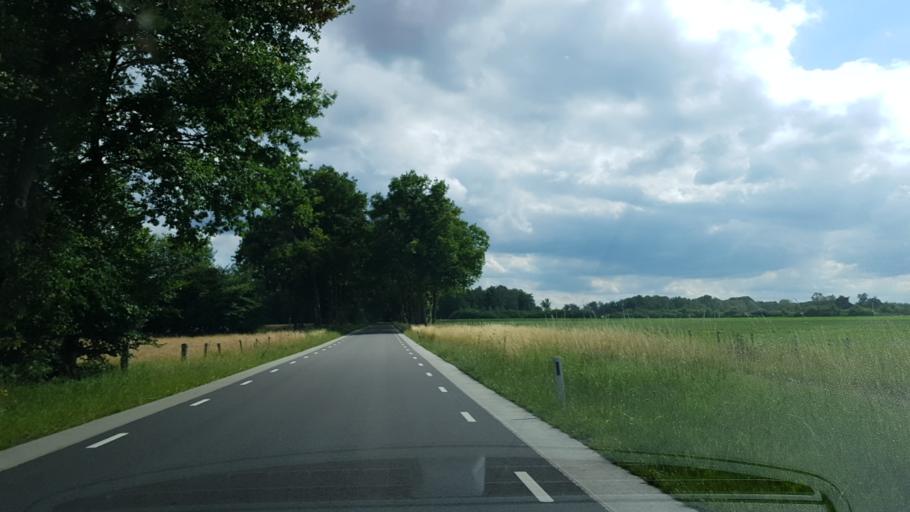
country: NL
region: Gelderland
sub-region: Gemeente Barneveld
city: Garderen
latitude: 52.2791
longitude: 5.7308
